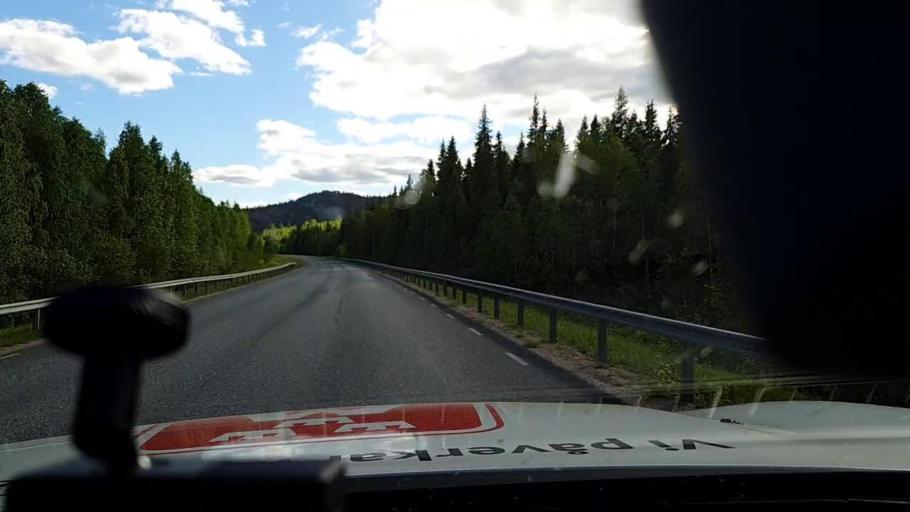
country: FI
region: Lapland
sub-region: Torniolaakso
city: Ylitornio
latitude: 66.3266
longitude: 23.6263
